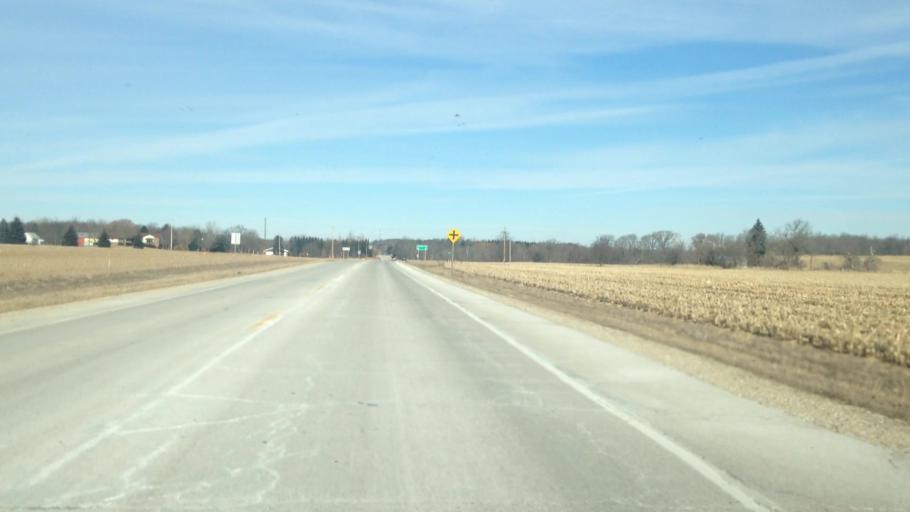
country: US
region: Wisconsin
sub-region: Washington County
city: Slinger
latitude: 43.2782
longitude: -88.2613
